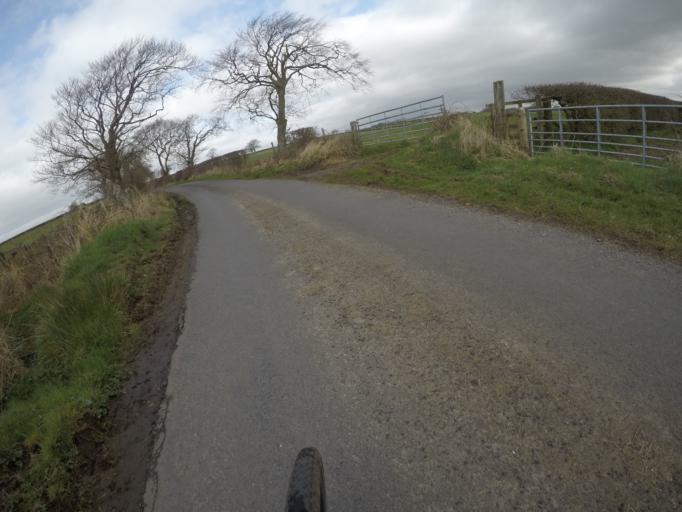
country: GB
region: Scotland
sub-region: North Ayrshire
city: Springside
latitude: 55.6641
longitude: -4.5910
